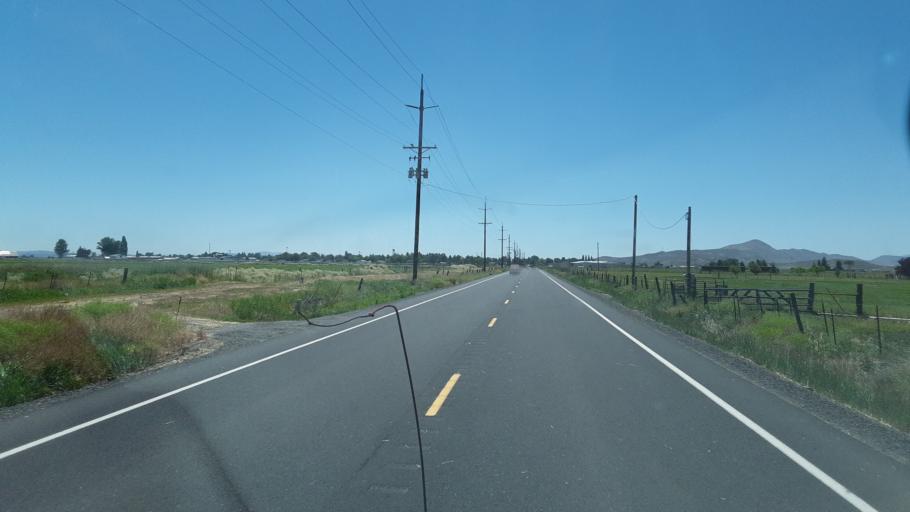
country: US
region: California
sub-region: Siskiyou County
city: Tulelake
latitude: 42.0356
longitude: -121.6189
